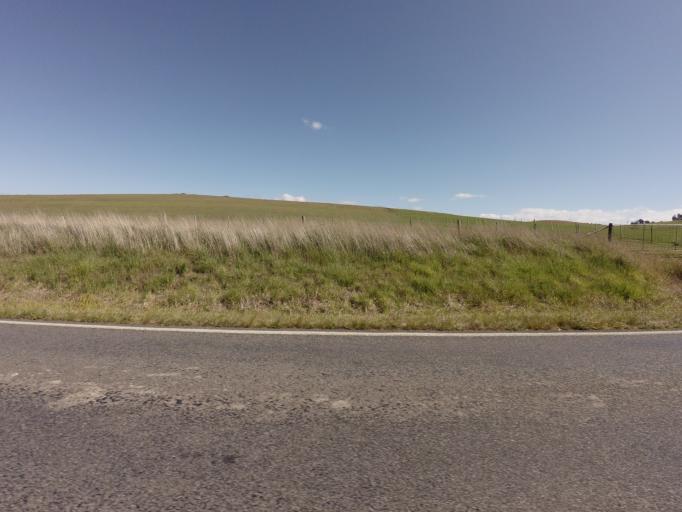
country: AU
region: Tasmania
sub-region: Derwent Valley
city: New Norfolk
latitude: -42.6498
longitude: 146.9293
